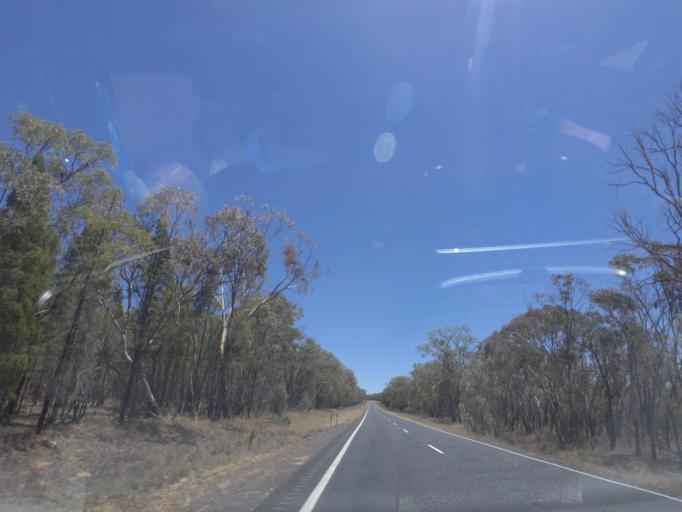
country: AU
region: New South Wales
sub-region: Warrumbungle Shire
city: Coonabarabran
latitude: -31.2006
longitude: 149.3440
